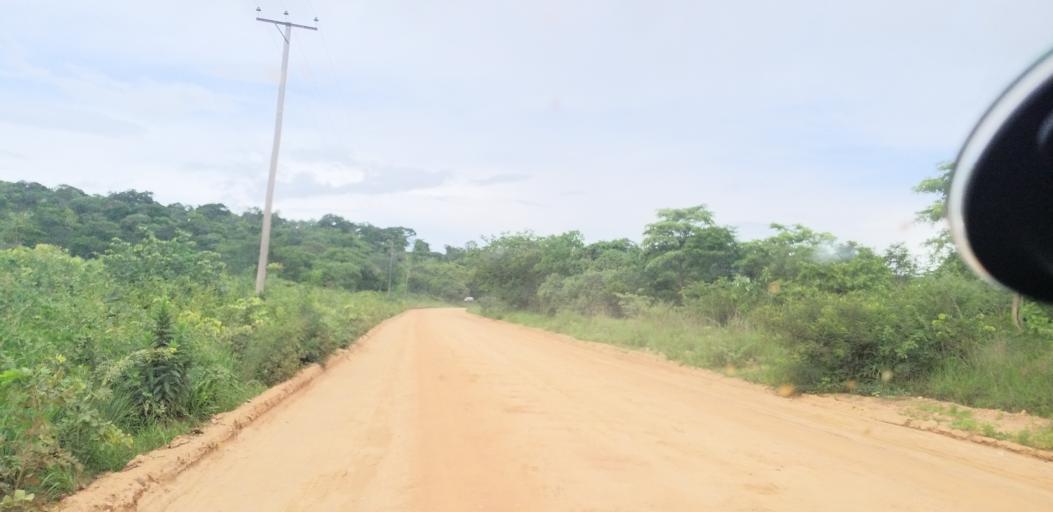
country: ZM
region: Lusaka
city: Chongwe
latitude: -15.1824
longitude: 28.4494
